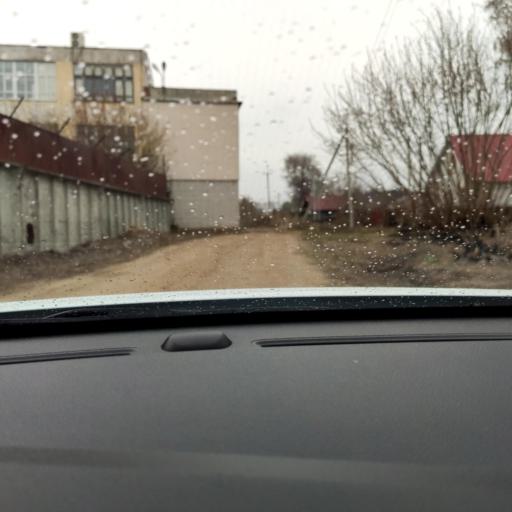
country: RU
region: Tatarstan
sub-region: Gorod Kazan'
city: Kazan
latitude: 55.7528
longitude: 49.1358
